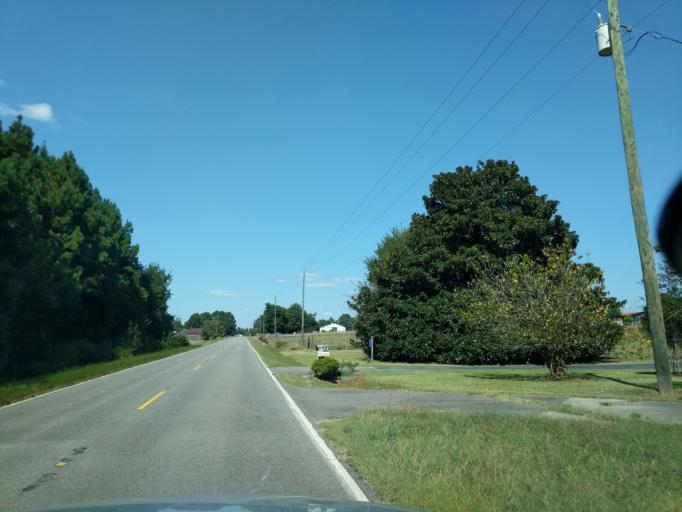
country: US
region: South Carolina
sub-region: Lexington County
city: Leesville
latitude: 33.9928
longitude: -81.5192
